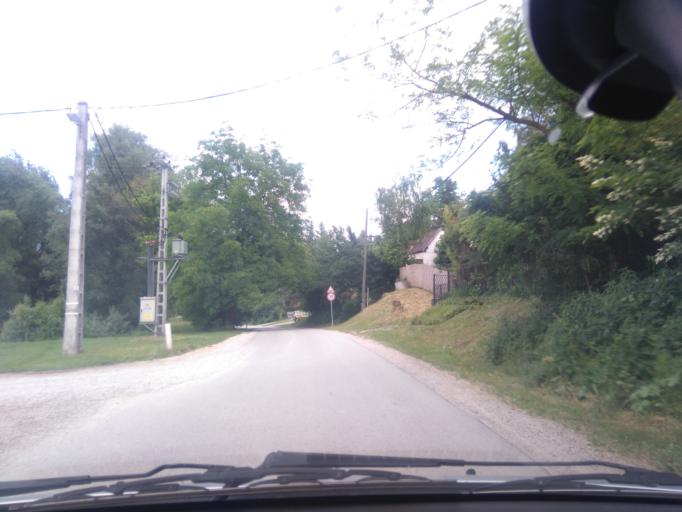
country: HU
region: Pest
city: Szob
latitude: 47.8074
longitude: 18.8107
